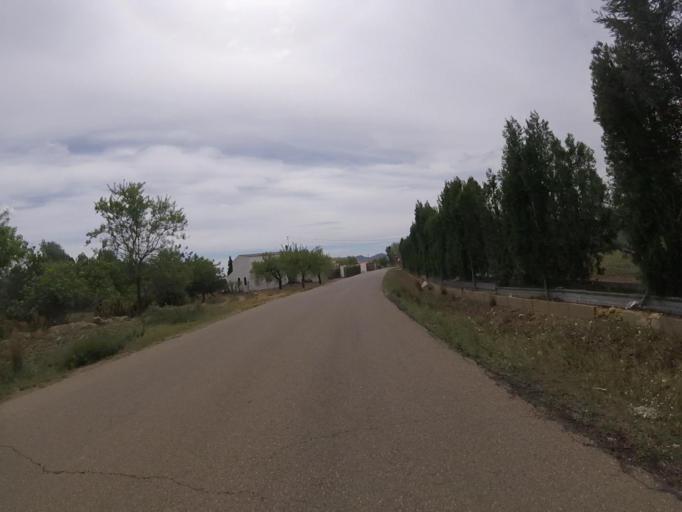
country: ES
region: Valencia
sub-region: Provincia de Castello
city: Benlloch
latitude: 40.1982
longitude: -0.0080
